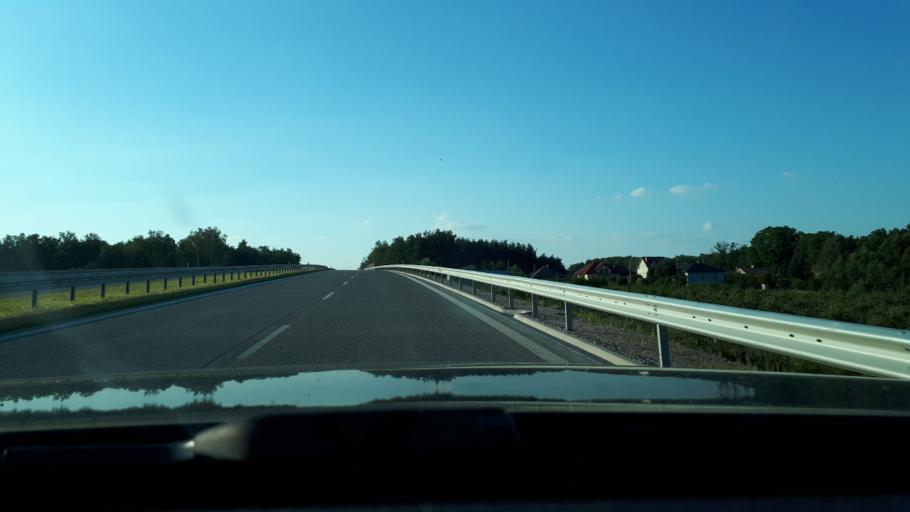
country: PL
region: Masovian Voivodeship
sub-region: Powiat piaseczynski
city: Baniocha
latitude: 51.9920
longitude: 21.1713
